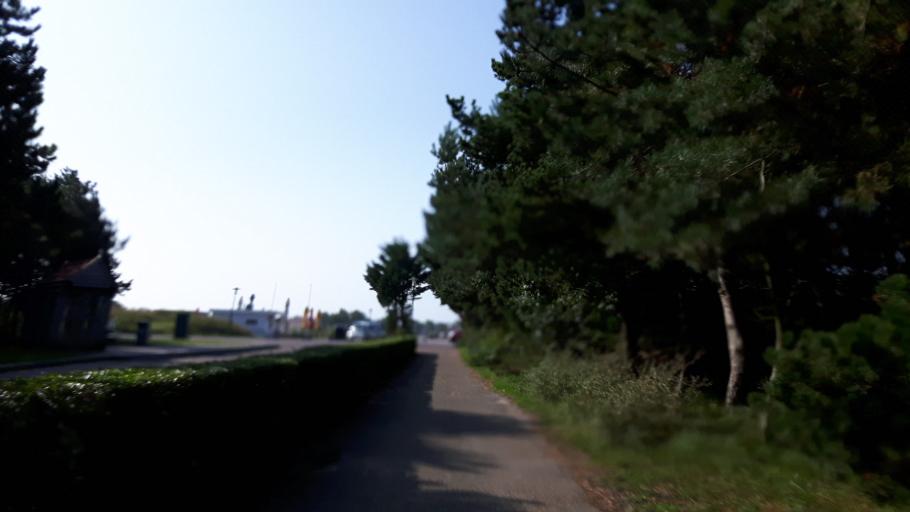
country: NL
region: Friesland
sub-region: Gemeente Ameland
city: Nes
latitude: 53.4542
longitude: 5.8030
